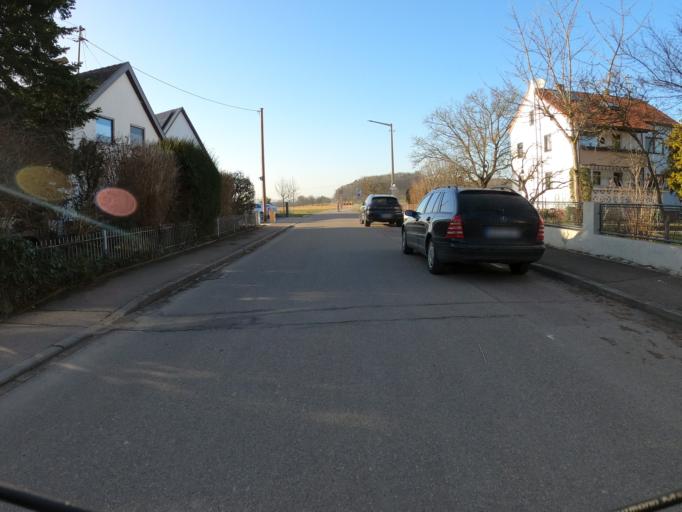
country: DE
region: Bavaria
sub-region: Swabia
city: Holzheim
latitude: 48.4024
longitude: 10.1039
